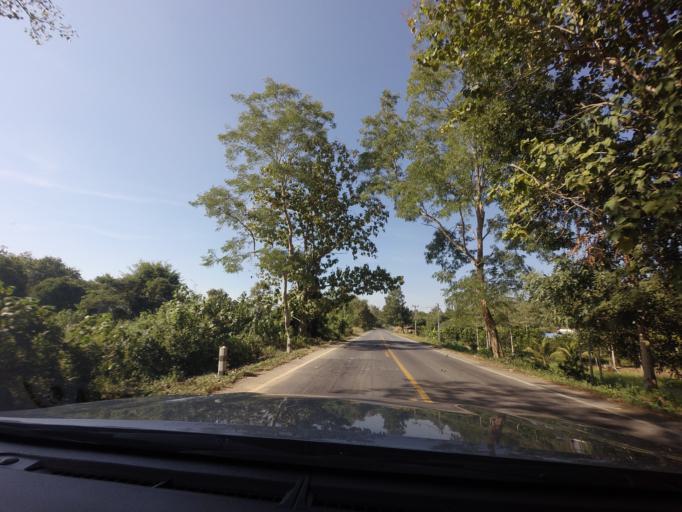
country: TH
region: Sukhothai
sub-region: Amphoe Si Satchanalai
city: Si Satchanalai
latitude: 17.6188
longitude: 99.7068
